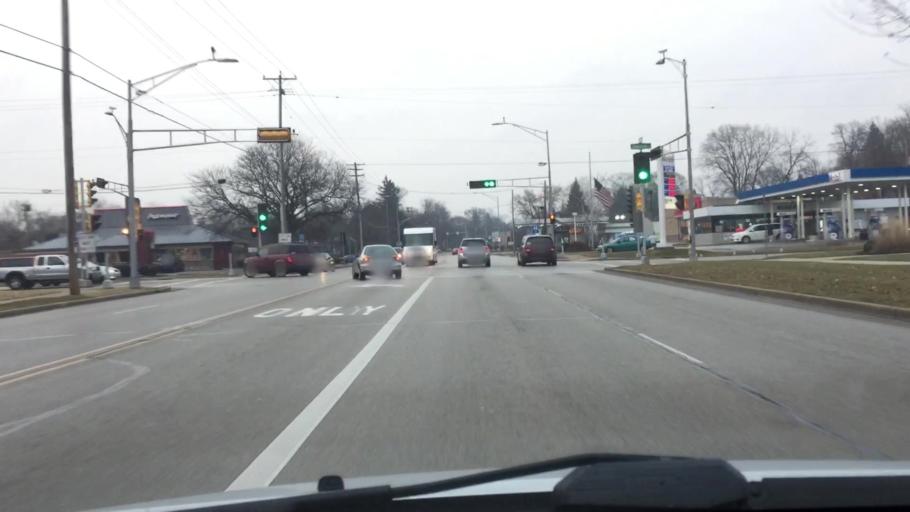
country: US
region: Wisconsin
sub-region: Waukesha County
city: Waukesha
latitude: 43.0219
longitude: -88.2564
